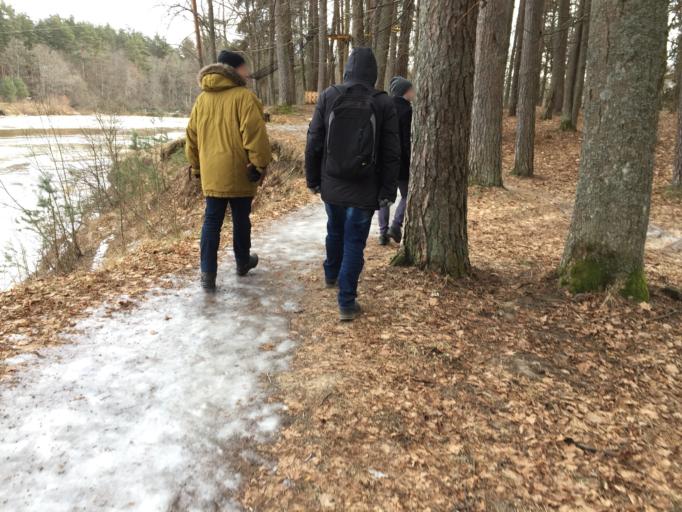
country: LV
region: Valmieras Rajons
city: Valmiera
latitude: 57.5384
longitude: 25.4435
